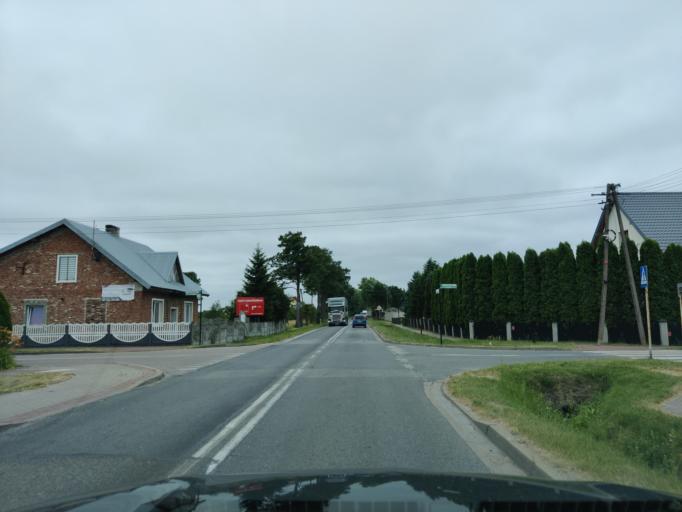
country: PL
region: Masovian Voivodeship
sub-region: Powiat ostrolecki
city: Myszyniec
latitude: 53.3832
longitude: 21.3385
